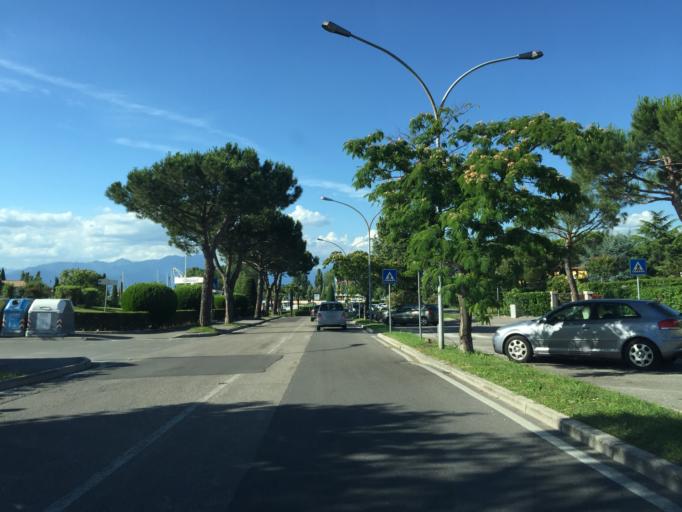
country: IT
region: Lombardy
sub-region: Provincia di Brescia
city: Sirmione
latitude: 45.4704
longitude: 10.6045
